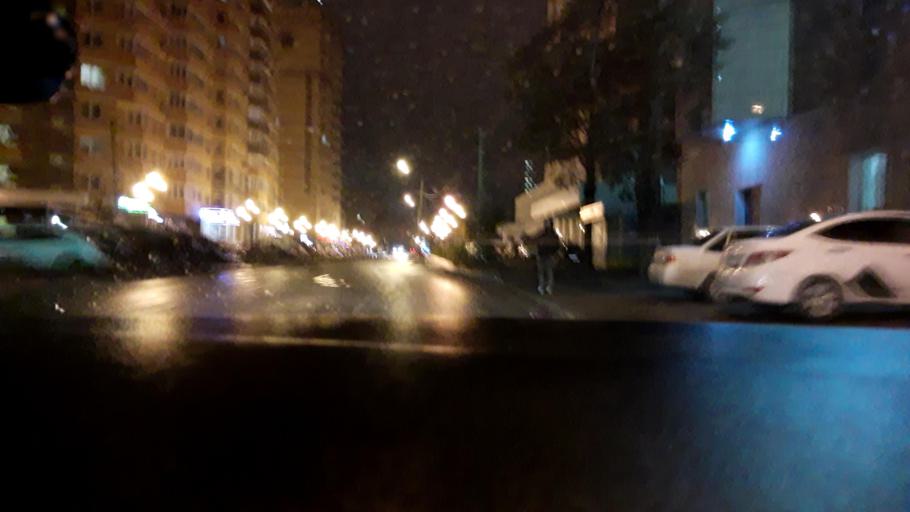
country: RU
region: Moskovskaya
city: Zheleznodorozhnyy
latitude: 55.7501
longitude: 37.9932
